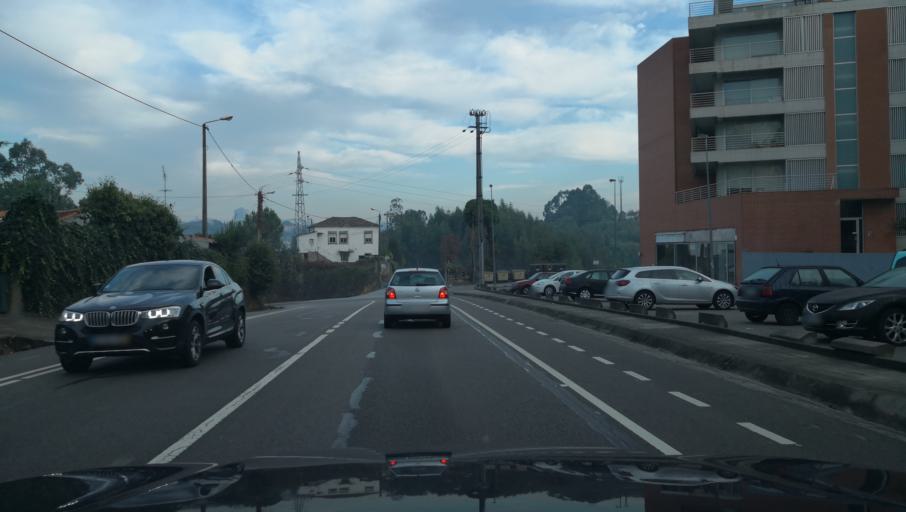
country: PT
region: Porto
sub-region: Gondomar
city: Valbom
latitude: 41.1461
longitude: -8.5679
